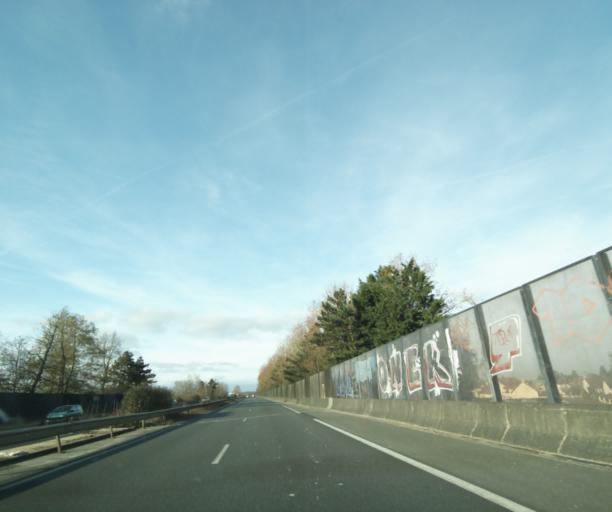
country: FR
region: Ile-de-France
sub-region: Departement des Yvelines
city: Le Perray-en-Yvelines
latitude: 48.6902
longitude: 1.8440
